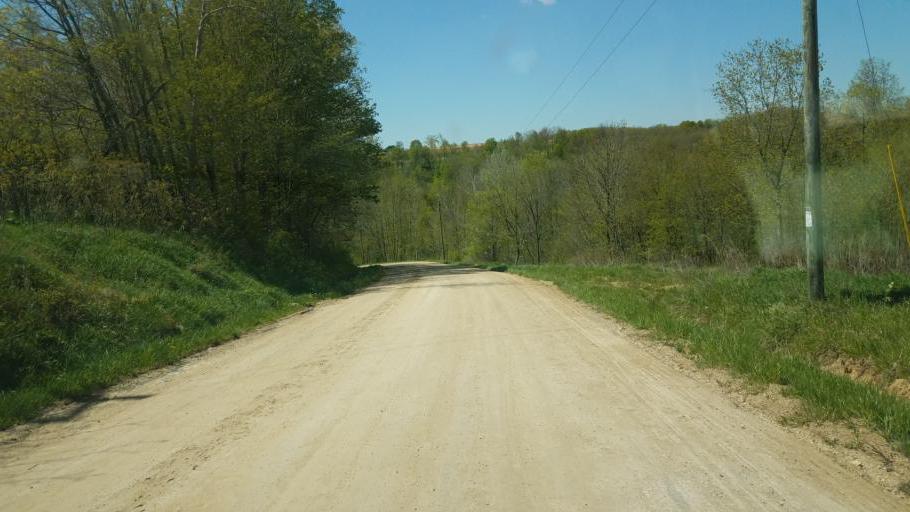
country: US
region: Wisconsin
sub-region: Vernon County
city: Hillsboro
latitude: 43.5960
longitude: -90.4096
